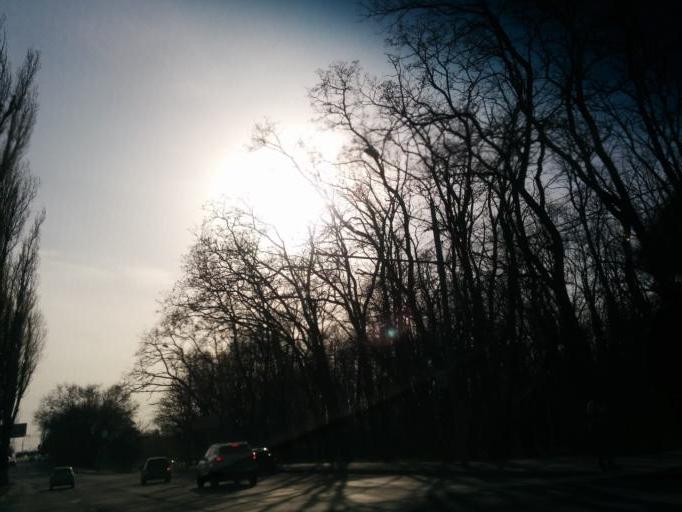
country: RU
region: Rostov
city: Imeni Chkalova
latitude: 47.2564
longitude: 39.7980
